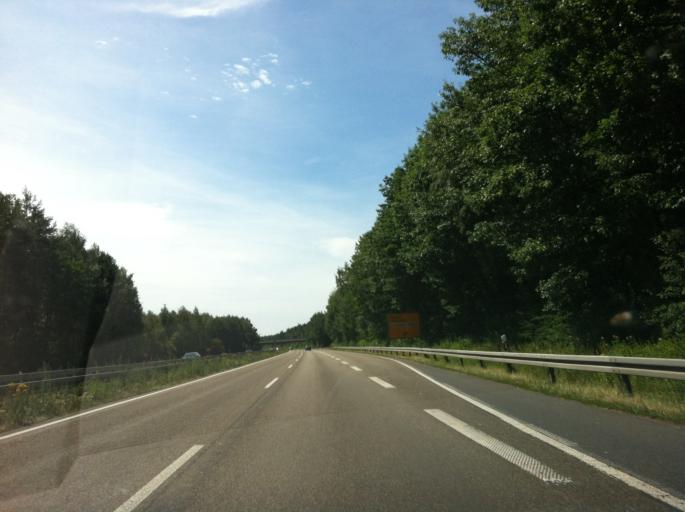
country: DE
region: Hesse
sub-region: Regierungsbezirk Darmstadt
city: Eppertshausen
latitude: 49.9858
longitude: 8.8737
